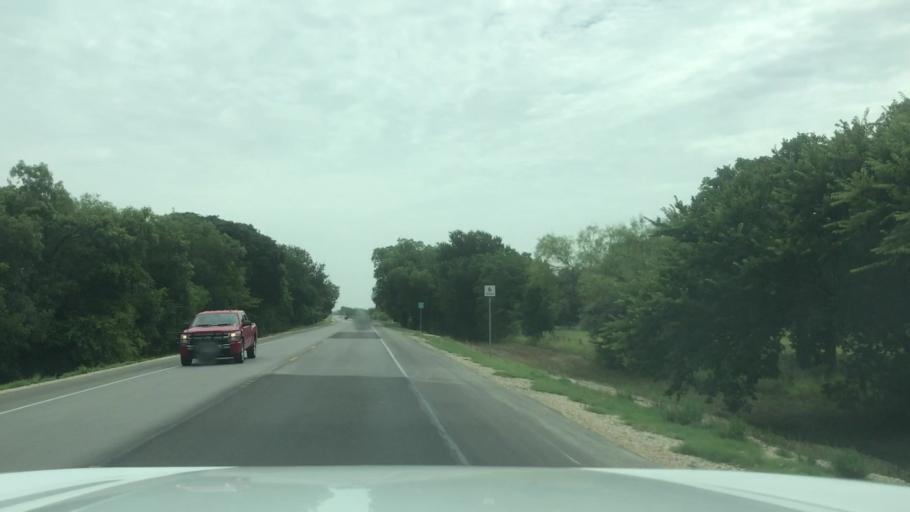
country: US
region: Texas
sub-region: Erath County
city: Dublin
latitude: 32.0885
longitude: -98.2978
